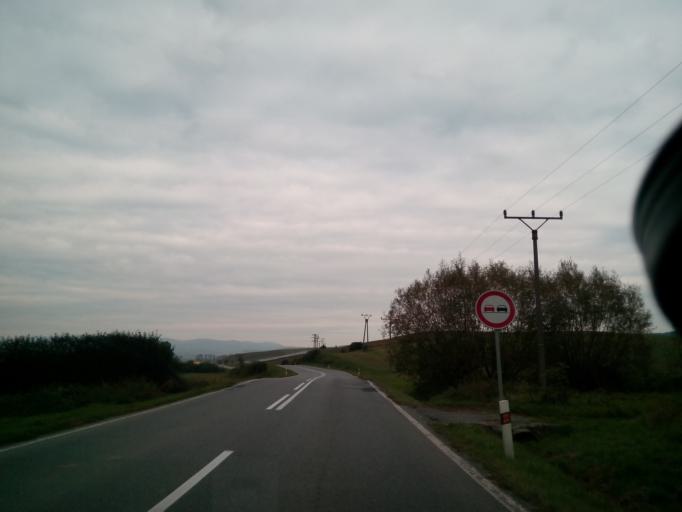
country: SK
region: Presovsky
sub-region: Okres Presov
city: Presov
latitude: 49.0645
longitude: 21.3414
